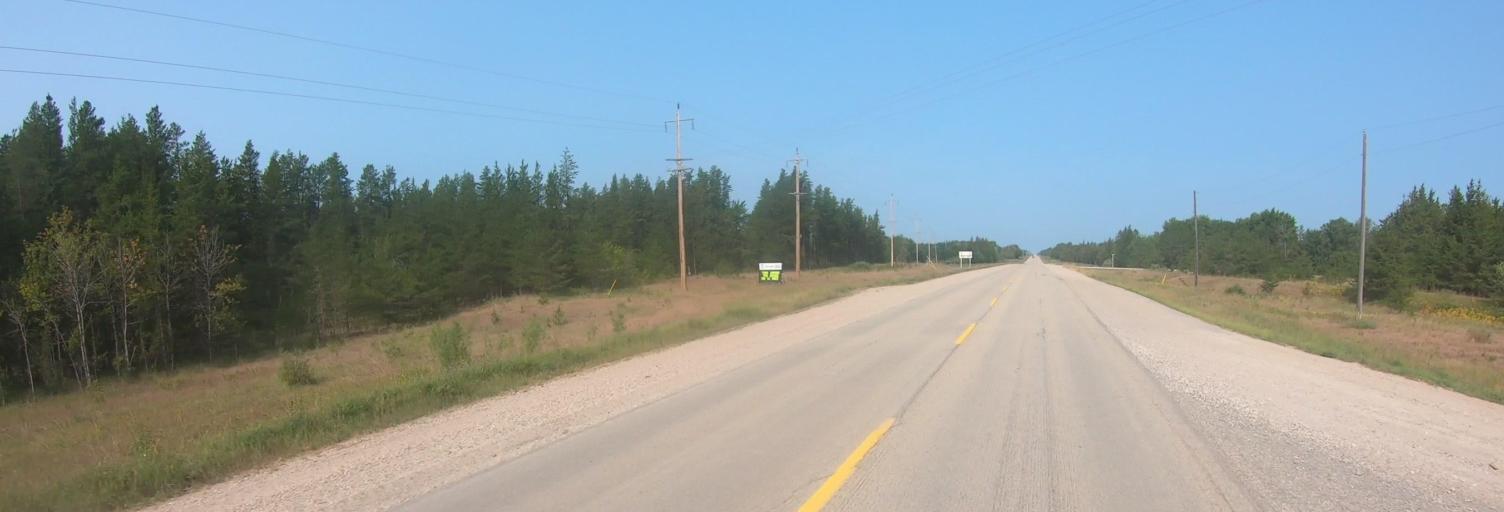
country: US
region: Minnesota
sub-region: Roseau County
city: Roseau
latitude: 49.0402
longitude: -95.7763
